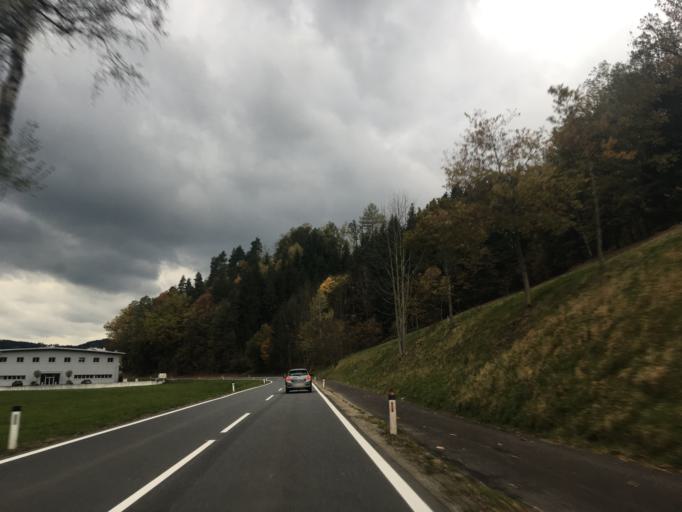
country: AT
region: Upper Austria
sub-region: Politischer Bezirk Urfahr-Umgebung
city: Herzogsdorf
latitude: 48.5391
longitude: 14.1365
